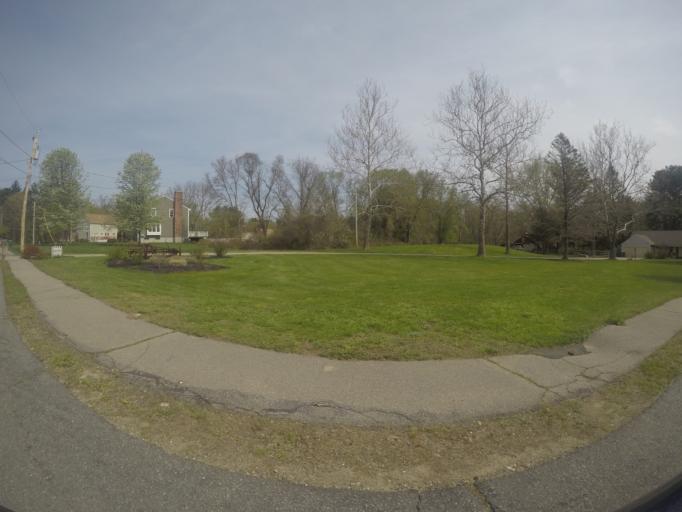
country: US
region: Massachusetts
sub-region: Bristol County
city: Easton
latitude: 42.0309
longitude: -71.1099
